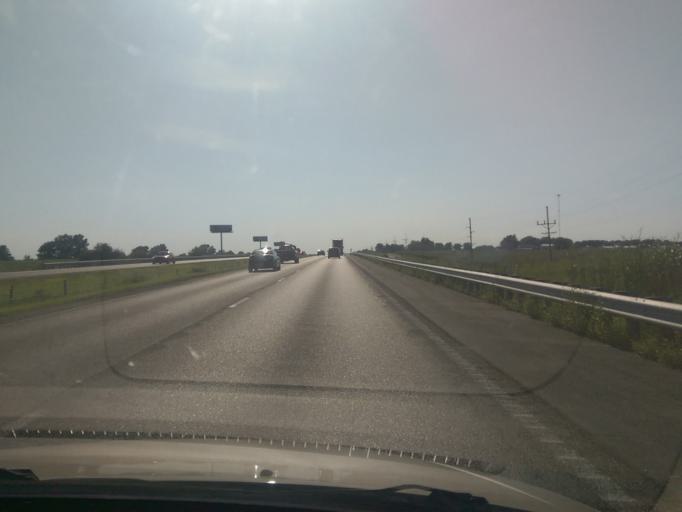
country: US
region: Missouri
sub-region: Lafayette County
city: Higginsville
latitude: 39.0014
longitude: -93.7537
